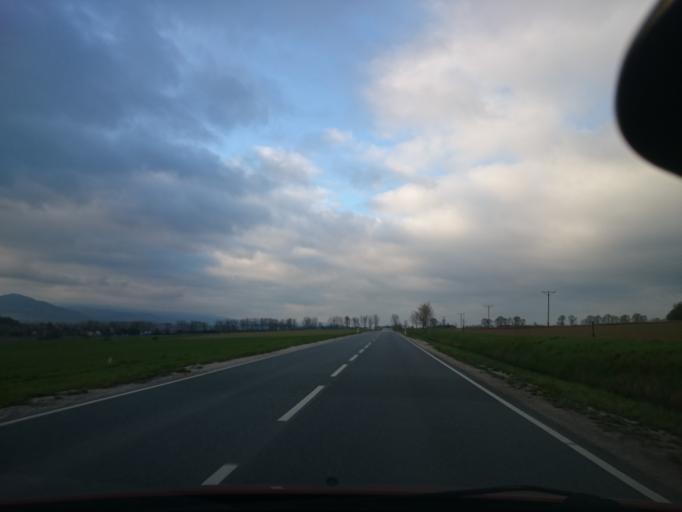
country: PL
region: Lower Silesian Voivodeship
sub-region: Powiat klodzki
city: Bystrzyca Klodzka
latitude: 50.2996
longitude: 16.6616
